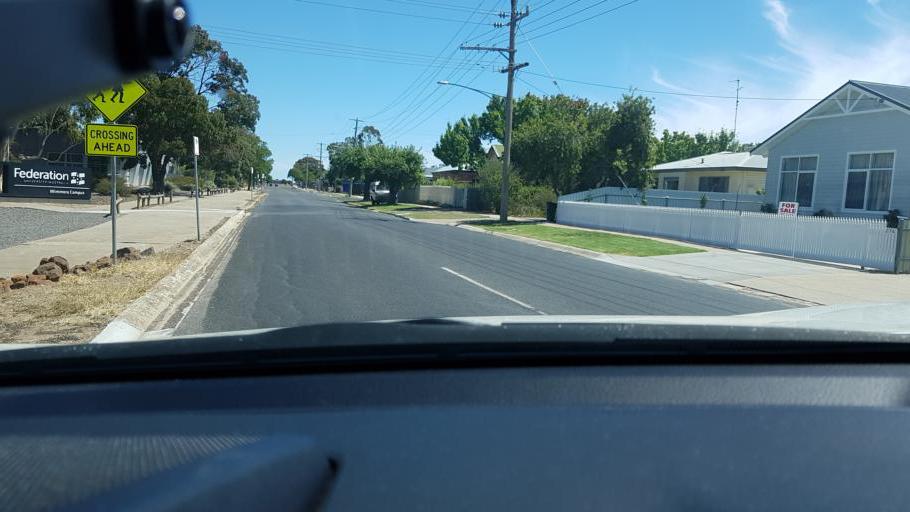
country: AU
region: Victoria
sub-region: Horsham
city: Horsham
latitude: -36.7118
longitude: 142.1875
